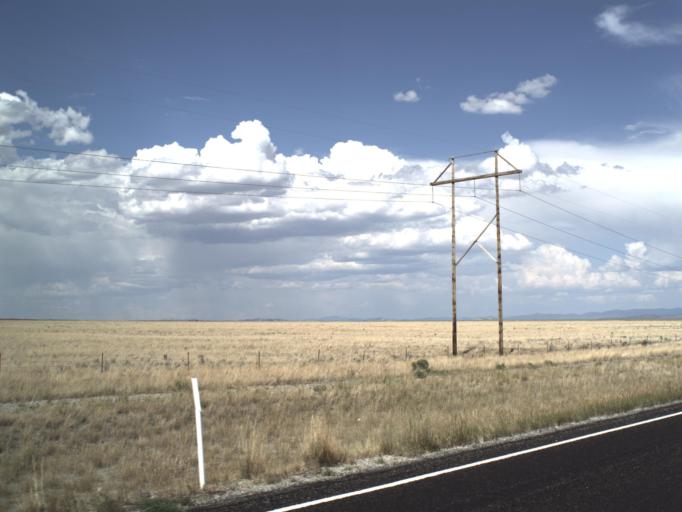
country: US
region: Idaho
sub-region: Power County
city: American Falls
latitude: 41.9683
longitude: -113.0975
